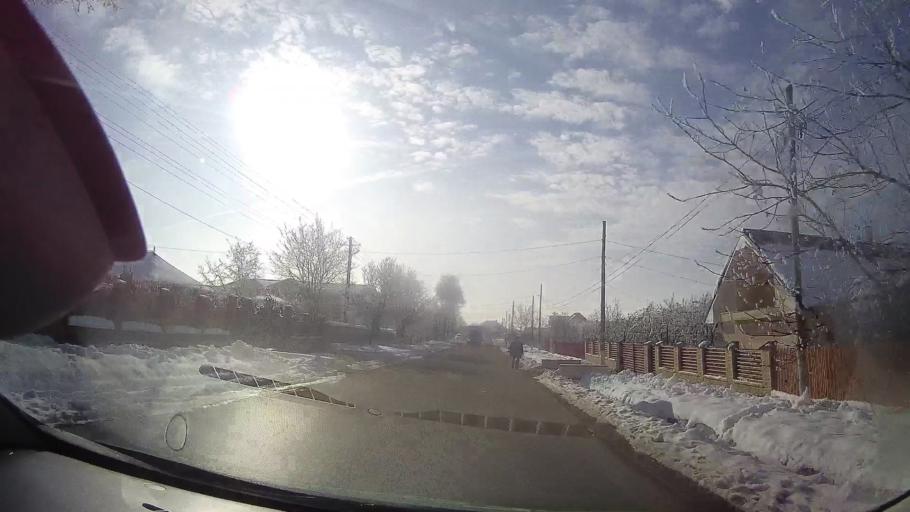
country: RO
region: Iasi
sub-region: Comuna Cristesti
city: Cristesti
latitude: 47.2520
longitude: 26.5690
